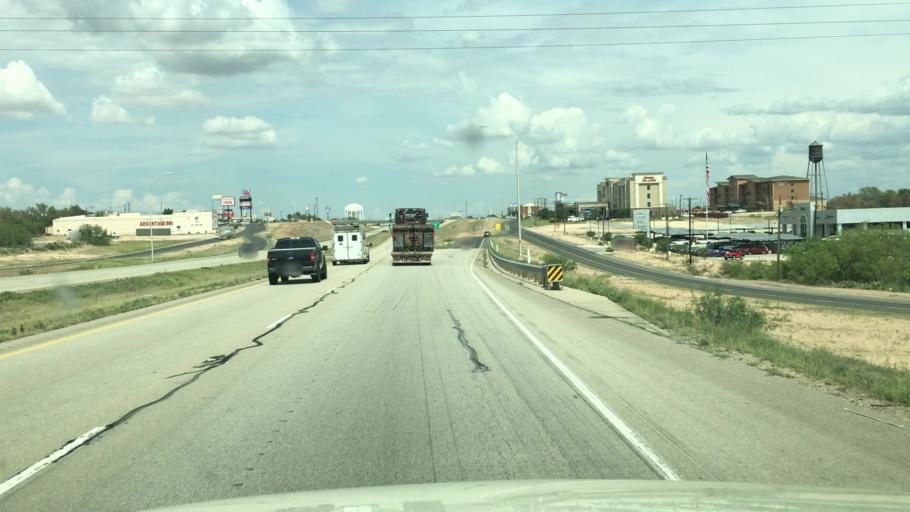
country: US
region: Texas
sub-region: Howard County
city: Big Spring
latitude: 32.2621
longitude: -101.4964
